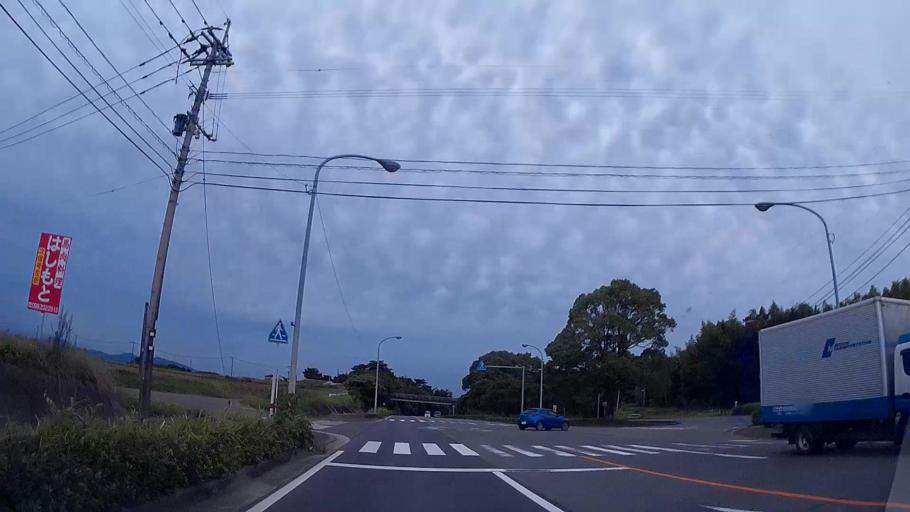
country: JP
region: Kumamoto
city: Ozu
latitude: 32.8499
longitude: 130.8593
